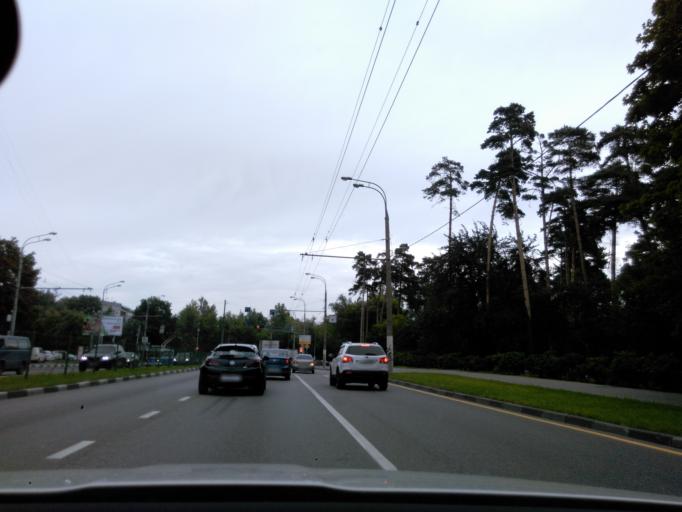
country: RU
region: Moscow
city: Tsaritsyno
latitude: 55.6268
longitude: 37.6571
